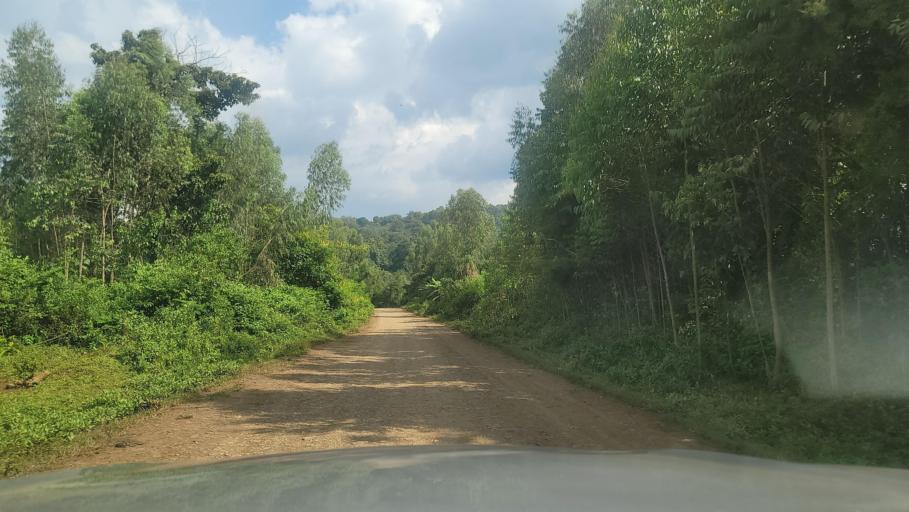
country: ET
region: Oromiya
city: Agaro
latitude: 7.7251
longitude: 36.2564
